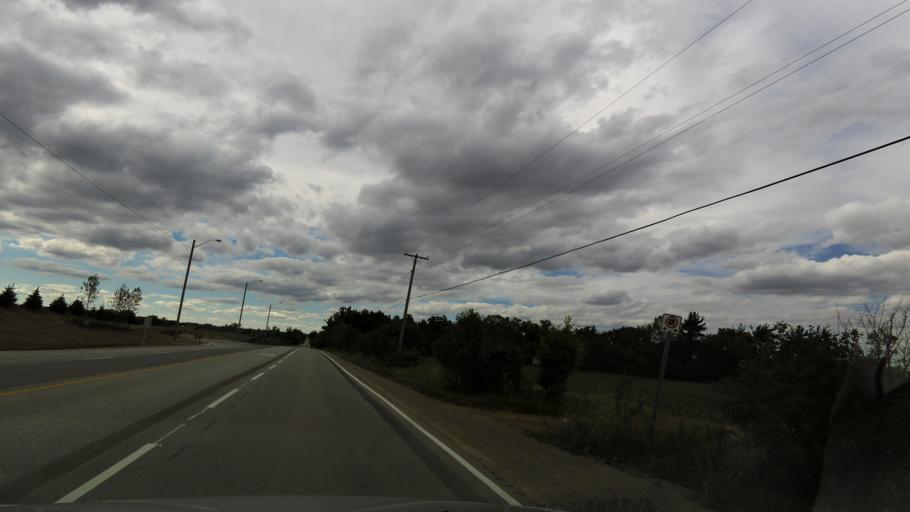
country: CA
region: Ontario
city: Brampton
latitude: 43.6204
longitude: -79.7900
